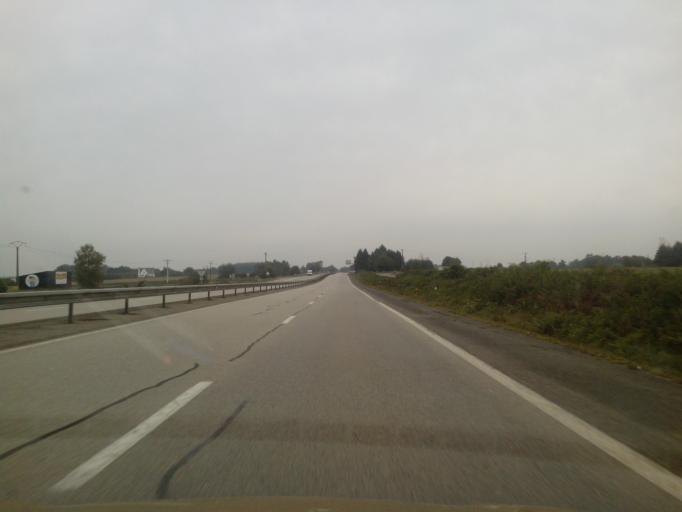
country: FR
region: Brittany
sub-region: Departement du Morbihan
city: Plumelin
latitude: 47.8924
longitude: -2.8905
